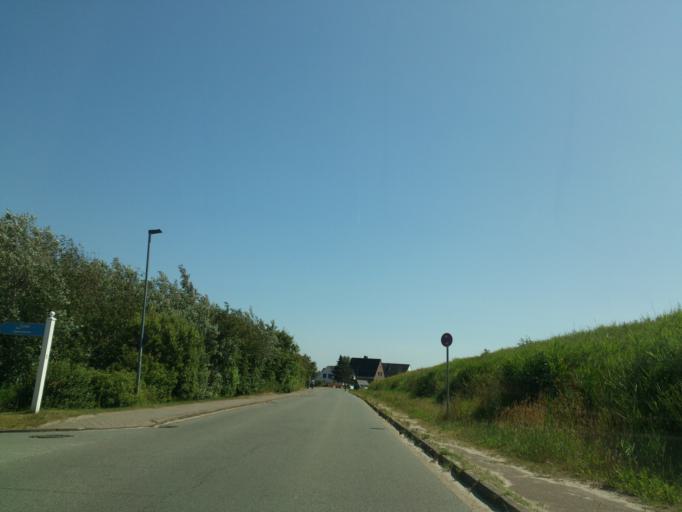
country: DE
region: Schleswig-Holstein
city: Sankt Peter-Ording
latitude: 54.3301
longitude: 8.6070
